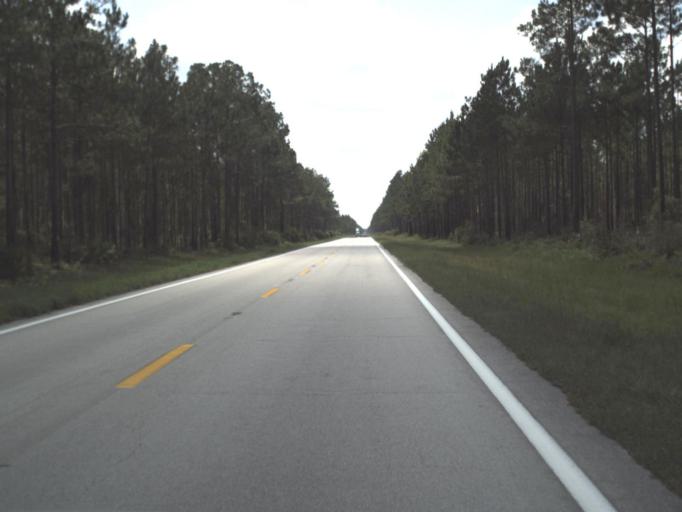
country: US
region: Florida
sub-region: Baker County
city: Macclenny
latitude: 30.5474
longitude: -82.3522
